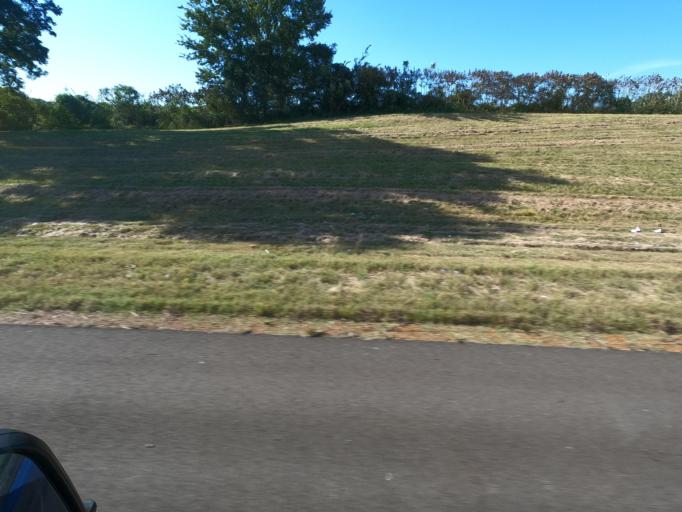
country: US
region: Tennessee
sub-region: Obion County
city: Troy
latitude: 36.3175
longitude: -89.1856
